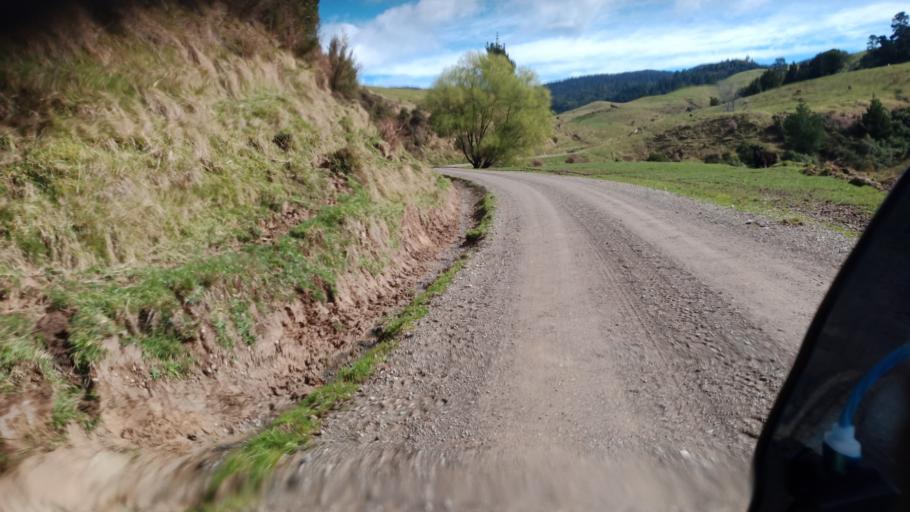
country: NZ
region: Hawke's Bay
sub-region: Wairoa District
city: Wairoa
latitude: -38.7358
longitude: 177.2993
